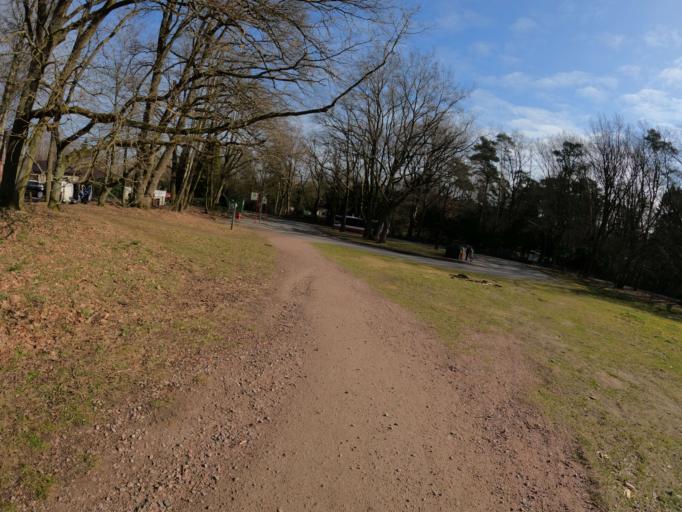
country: DE
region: Lower Saxony
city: Neu Wulmstorf
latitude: 53.4492
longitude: 9.8677
